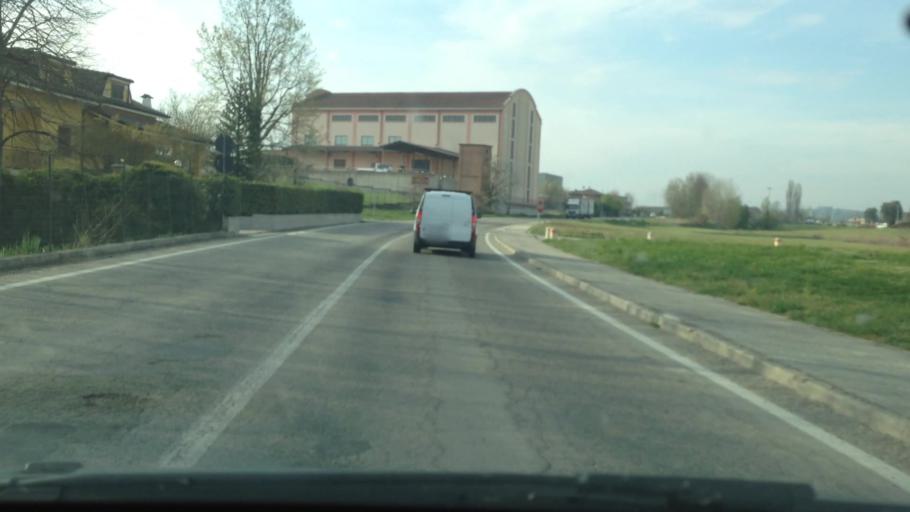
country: IT
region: Piedmont
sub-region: Provincia di Asti
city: San Damiano d'Asti
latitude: 44.8303
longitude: 8.0601
